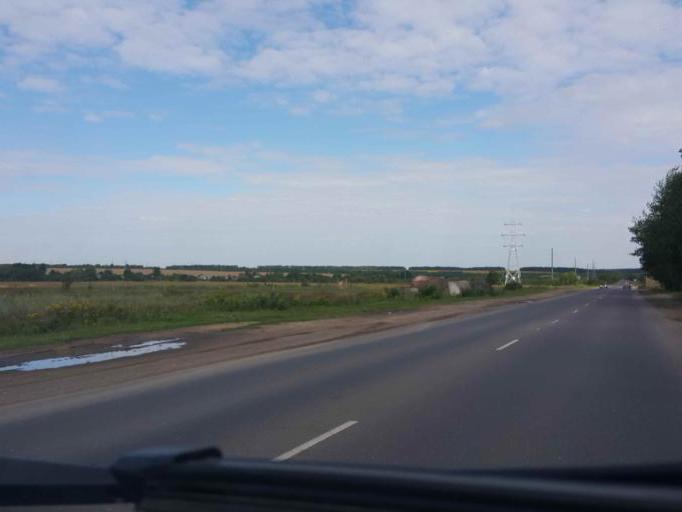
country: RU
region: Tambov
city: Bokino
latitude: 52.6417
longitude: 41.4264
